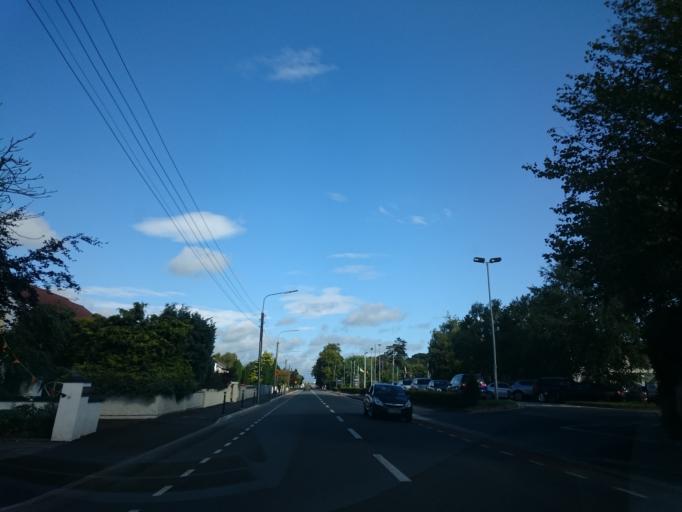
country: IE
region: Leinster
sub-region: Kilkenny
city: Kilkenny
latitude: 52.6635
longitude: -7.2510
